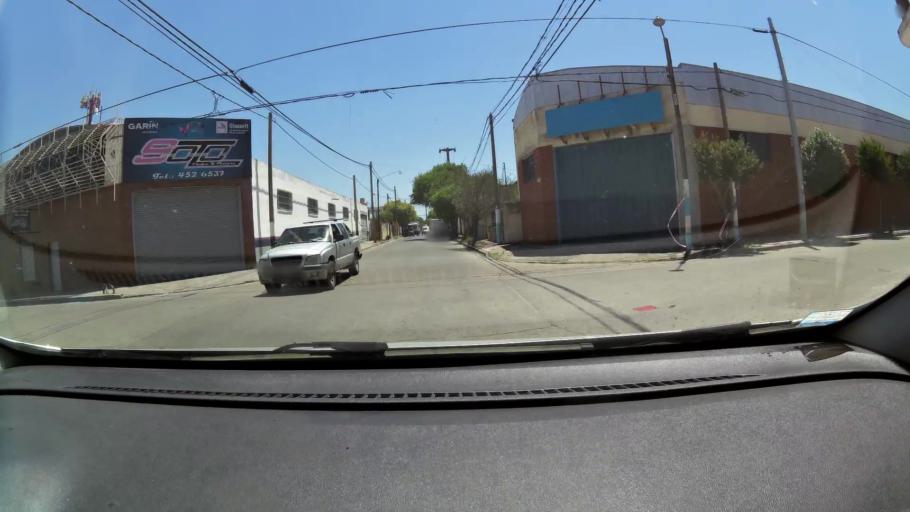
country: AR
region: Cordoba
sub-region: Departamento de Capital
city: Cordoba
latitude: -31.3904
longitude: -64.1441
